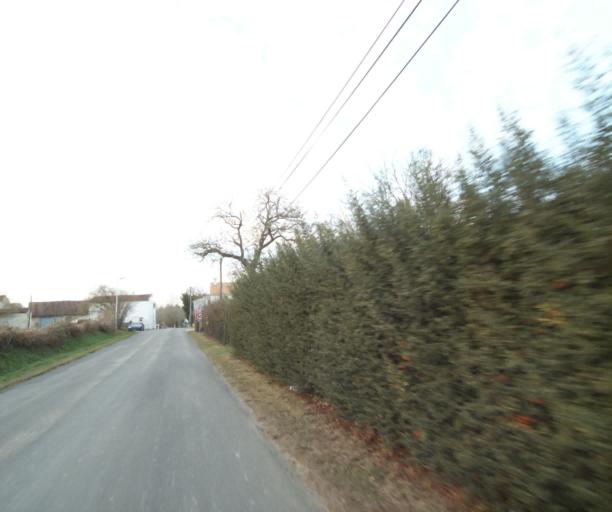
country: FR
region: Poitou-Charentes
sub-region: Departement de la Charente-Maritime
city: Les Gonds
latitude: 45.7182
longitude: -0.6270
